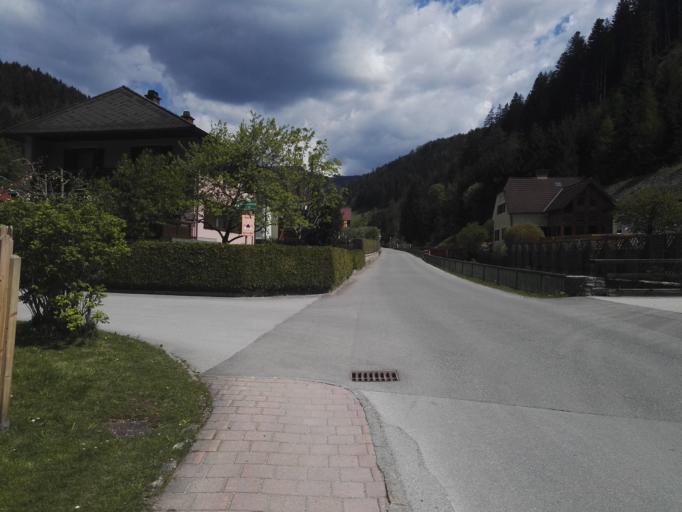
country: AT
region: Styria
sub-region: Politischer Bezirk Bruck-Muerzzuschlag
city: Allerheiligen im Muerztal
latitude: 47.3943
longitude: 15.4313
